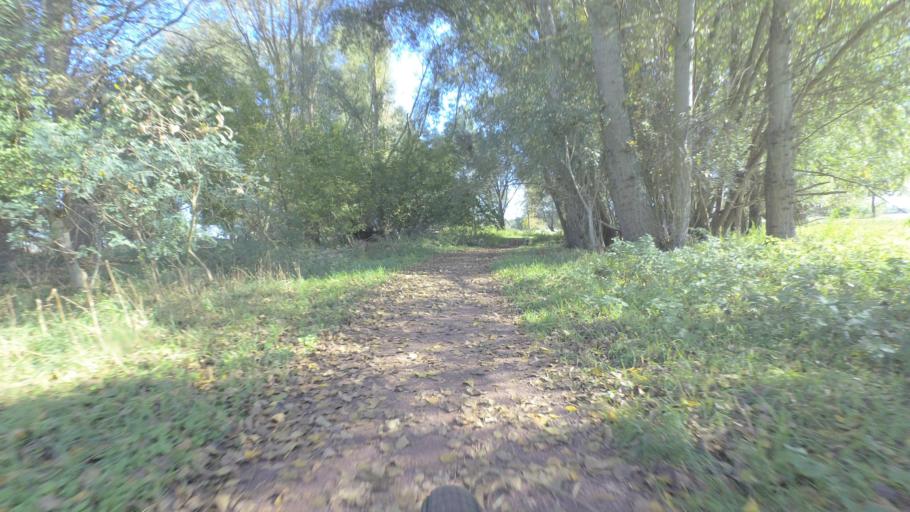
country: DE
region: Brandenburg
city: Rangsdorf
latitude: 52.2798
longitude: 13.4212
